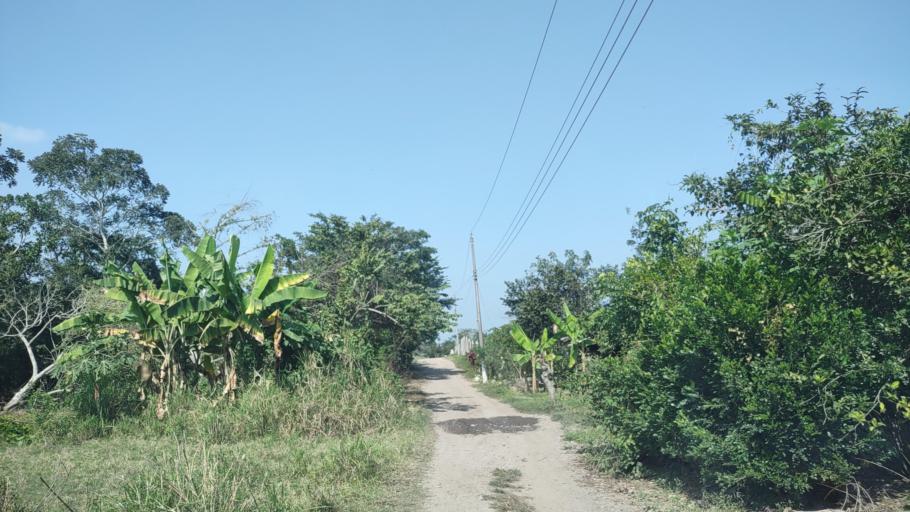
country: MX
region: Puebla
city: Espinal
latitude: 20.2615
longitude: -97.3078
